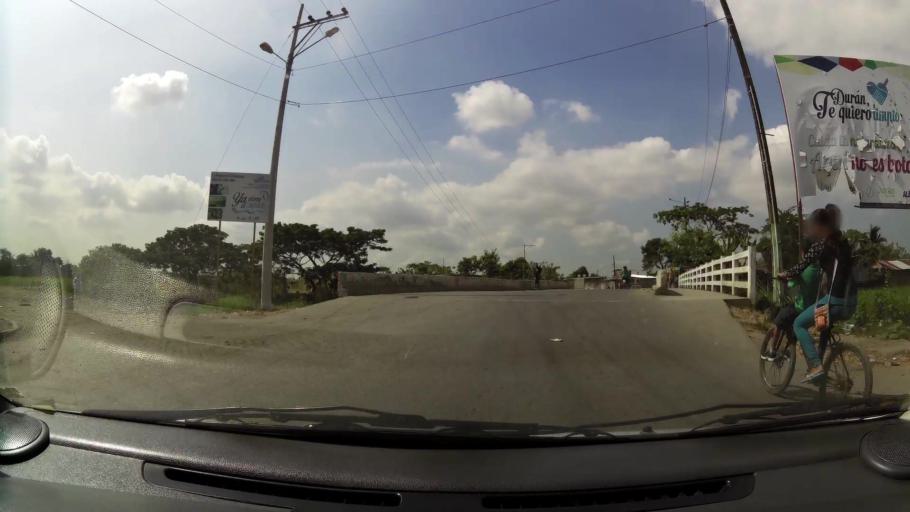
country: EC
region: Guayas
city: Eloy Alfaro
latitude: -2.1502
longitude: -79.8290
